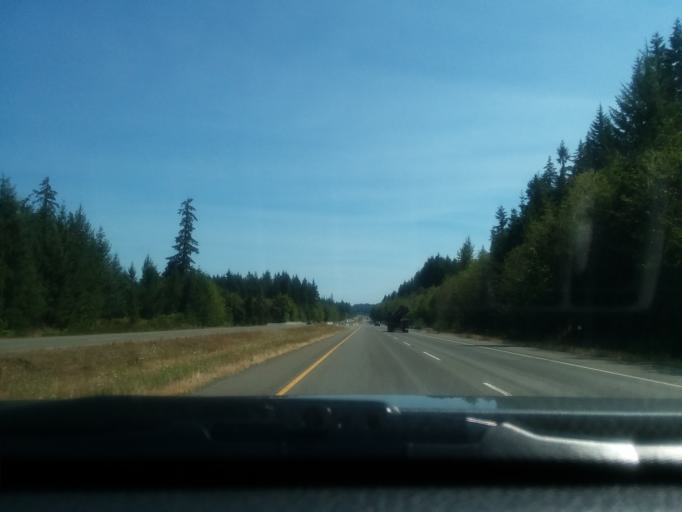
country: CA
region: British Columbia
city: Port Alberni
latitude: 49.4461
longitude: -124.7669
